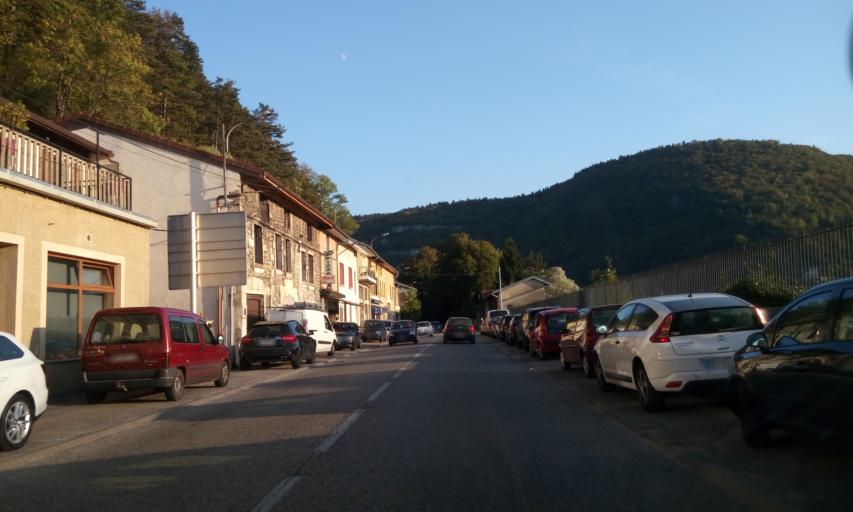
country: FR
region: Rhone-Alpes
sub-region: Departement de l'Ain
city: Montreal-la-Cluse
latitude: 46.1696
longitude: 5.5775
